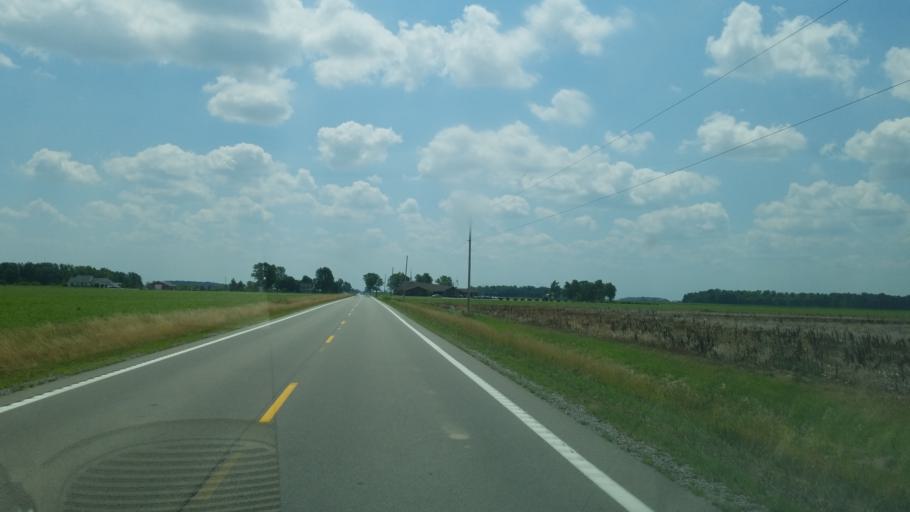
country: US
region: Ohio
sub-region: Henry County
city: Deshler
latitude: 41.2589
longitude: -83.9404
